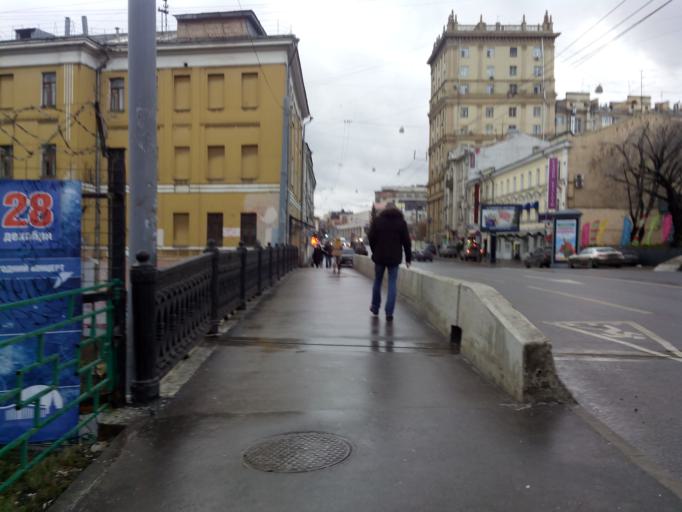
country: RU
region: Moscow
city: Taganskiy
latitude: 55.7648
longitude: 37.6587
